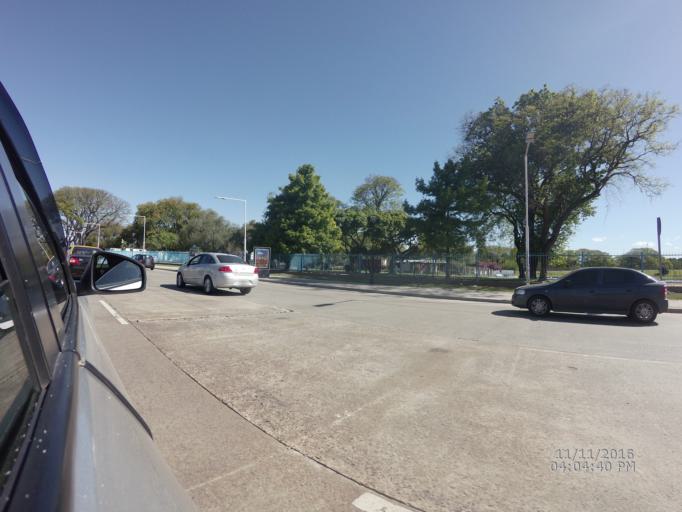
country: AR
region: Buenos Aires F.D.
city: Retiro
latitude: -34.5690
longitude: -58.4007
